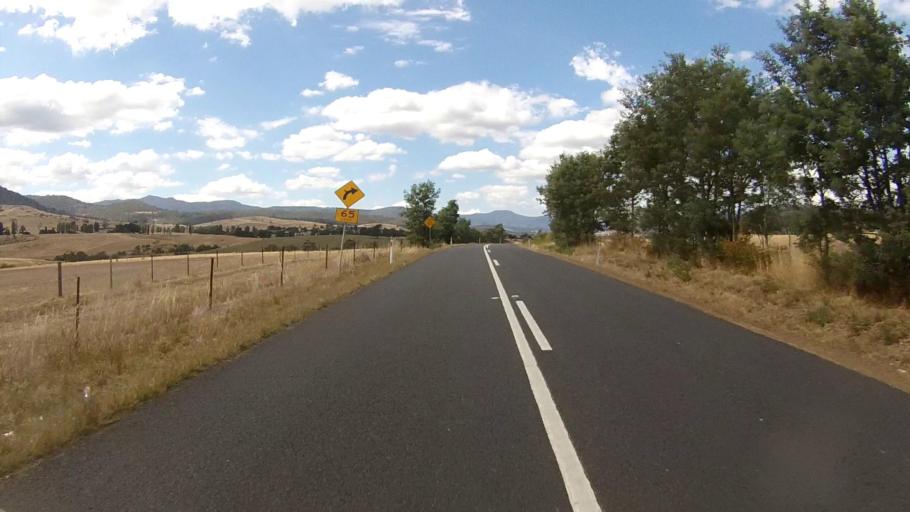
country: AU
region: Tasmania
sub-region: Derwent Valley
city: New Norfolk
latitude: -42.7539
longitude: 146.9806
